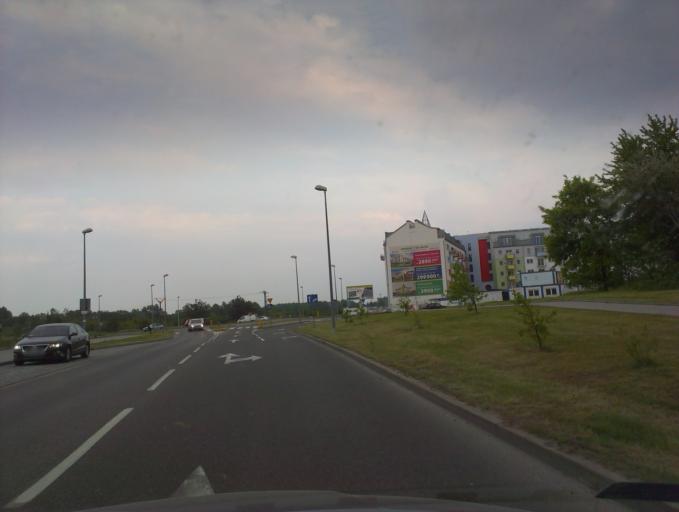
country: PL
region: West Pomeranian Voivodeship
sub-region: Koszalin
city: Koszalin
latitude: 54.1785
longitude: 16.2071
